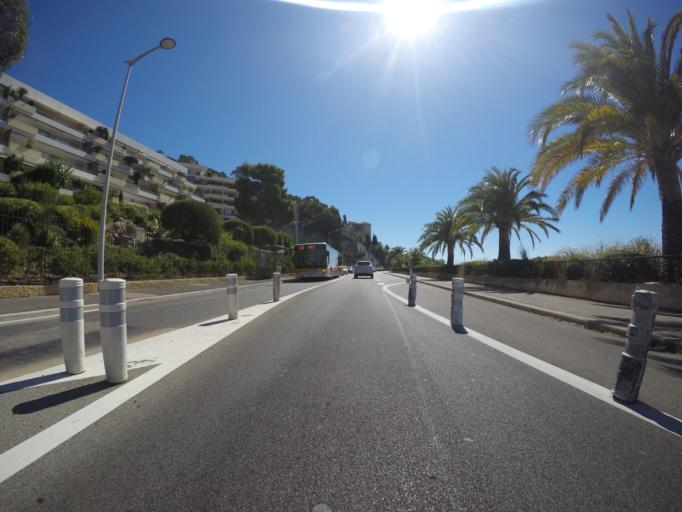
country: FR
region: Provence-Alpes-Cote d'Azur
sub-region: Departement des Alpes-Maritimes
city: Villefranche-sur-Mer
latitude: 43.6869
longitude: 7.3012
